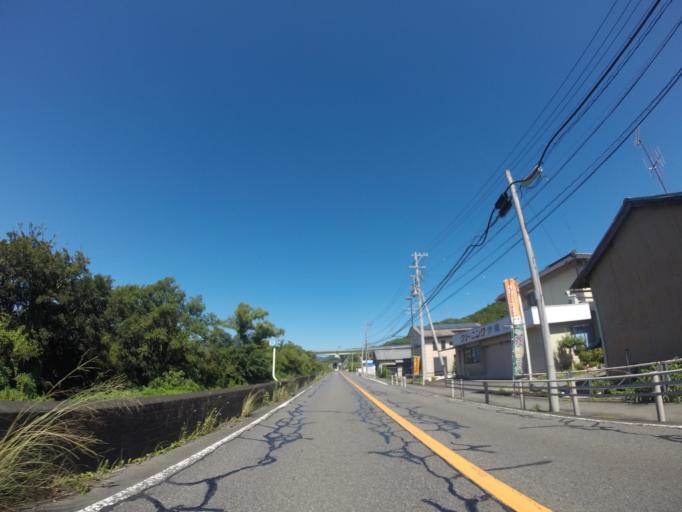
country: JP
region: Shizuoka
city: Kanaya
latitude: 34.8517
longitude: 138.1401
